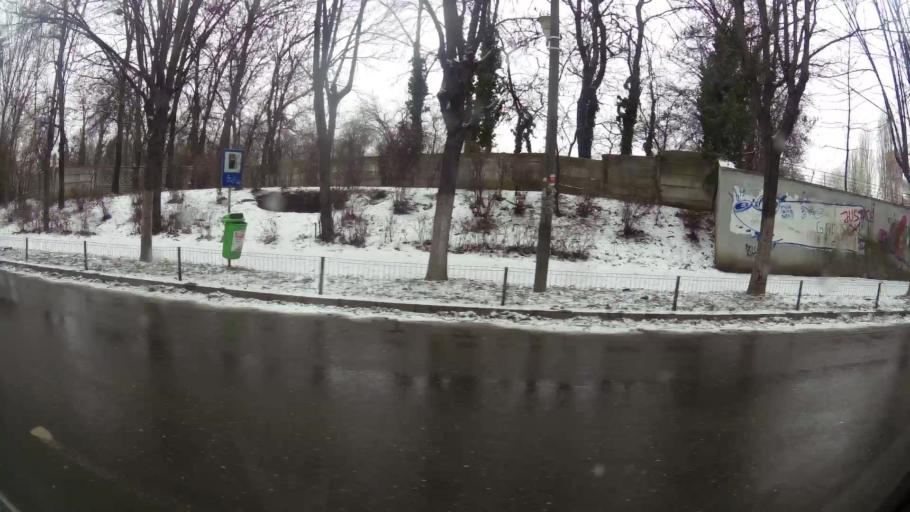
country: RO
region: Prahova
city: Ploiesti
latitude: 44.9562
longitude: 26.0069
